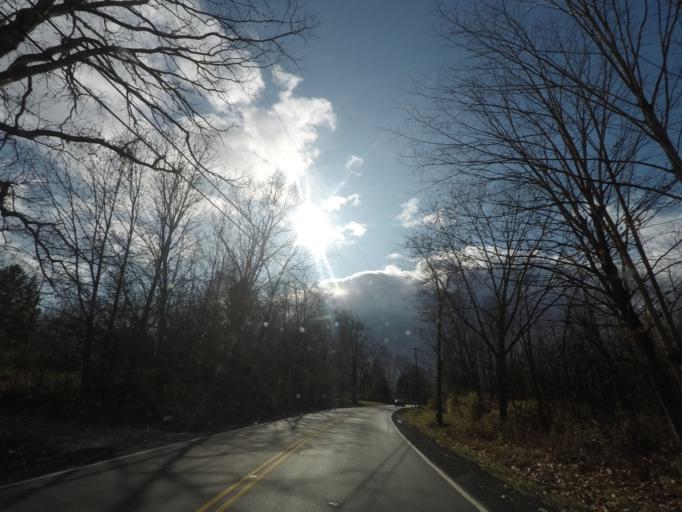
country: US
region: New York
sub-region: Saratoga County
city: Country Knolls
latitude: 42.9367
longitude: -73.8512
